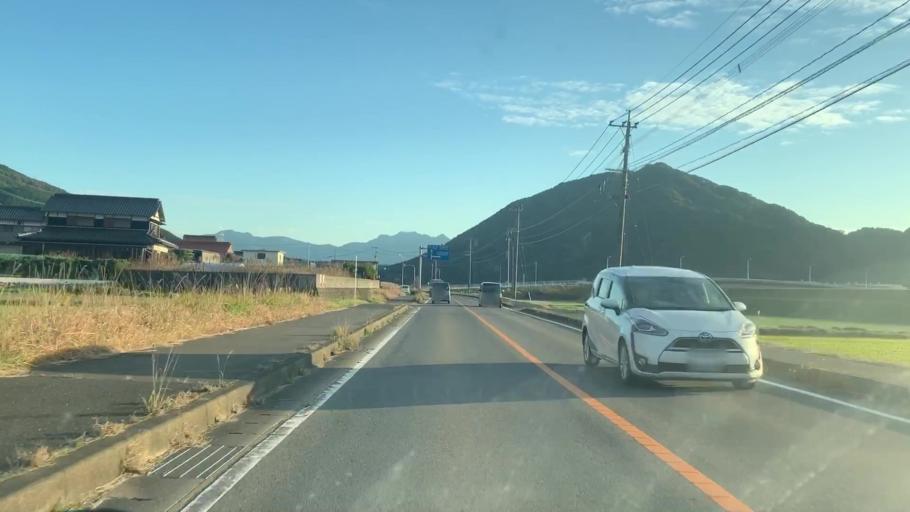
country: JP
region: Saga Prefecture
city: Karatsu
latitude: 33.3766
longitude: 129.9997
